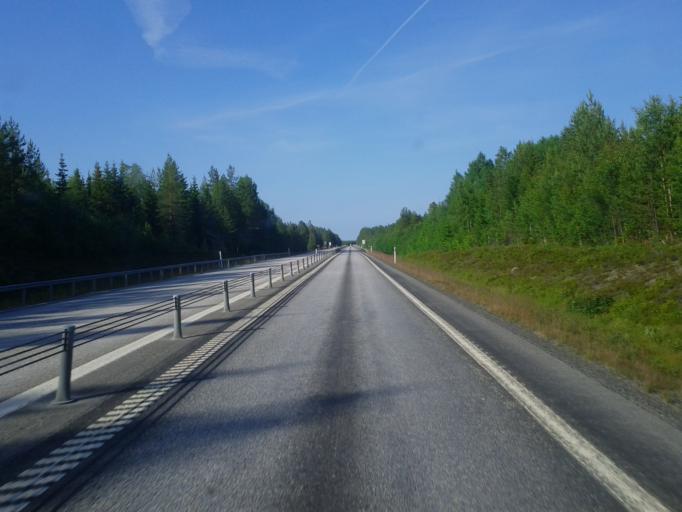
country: SE
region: Vaesterbotten
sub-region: Umea Kommun
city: Saevar
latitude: 63.9703
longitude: 20.7110
